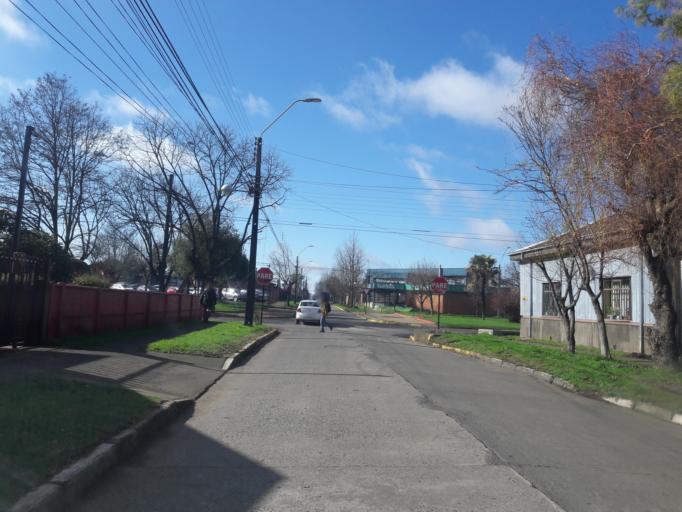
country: CL
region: Araucania
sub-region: Provincia de Malleco
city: Victoria
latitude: -38.2325
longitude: -72.3369
